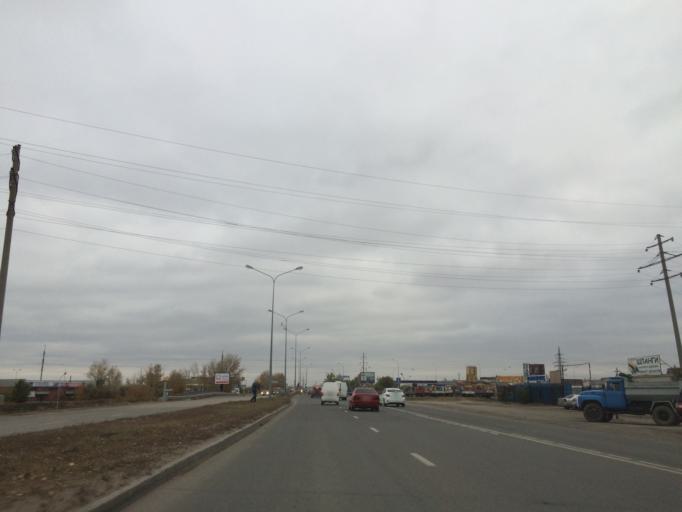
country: KZ
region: Astana Qalasy
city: Astana
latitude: 51.1973
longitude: 71.4743
